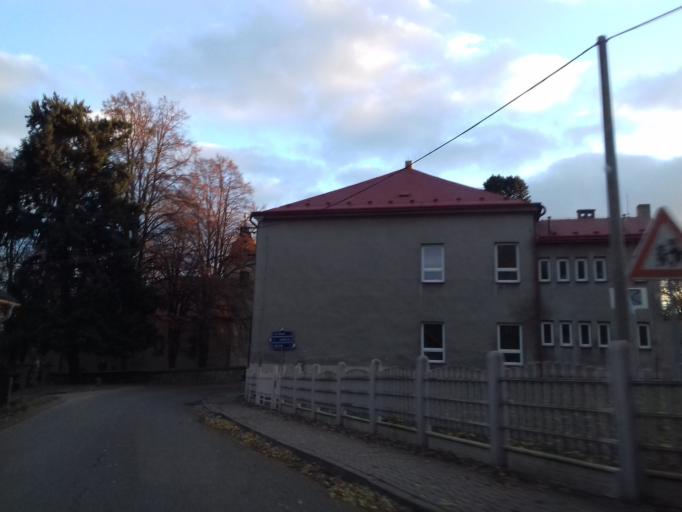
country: CZ
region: Pardubicky
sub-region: Okres Chrudim
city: Skutec
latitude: 49.7996
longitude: 15.9639
